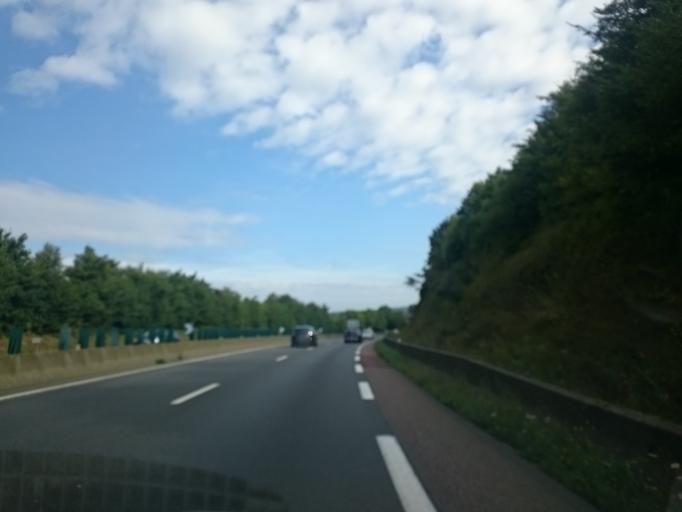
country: FR
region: Lower Normandy
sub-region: Departement de la Manche
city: Avranches
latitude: 48.6856
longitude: -1.3745
